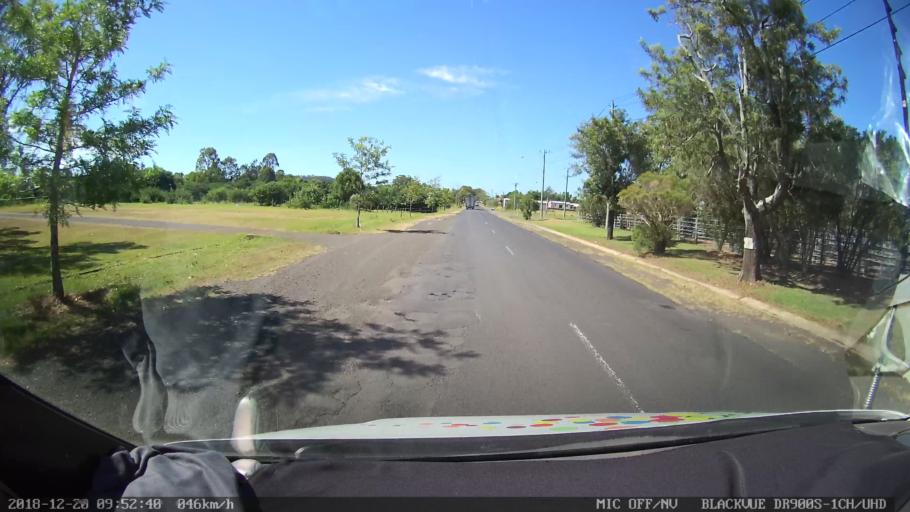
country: AU
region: New South Wales
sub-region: Lismore Municipality
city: Lismore
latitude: -28.7974
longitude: 153.2708
